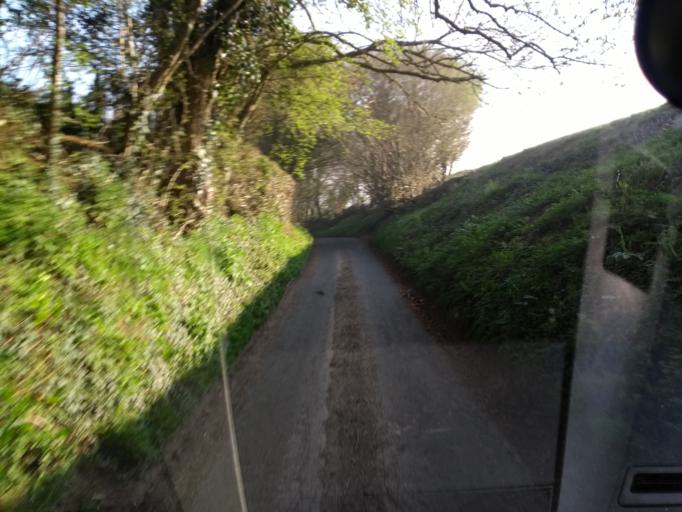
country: GB
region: England
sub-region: Somerset
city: Merriott
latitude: 50.9133
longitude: -2.8191
